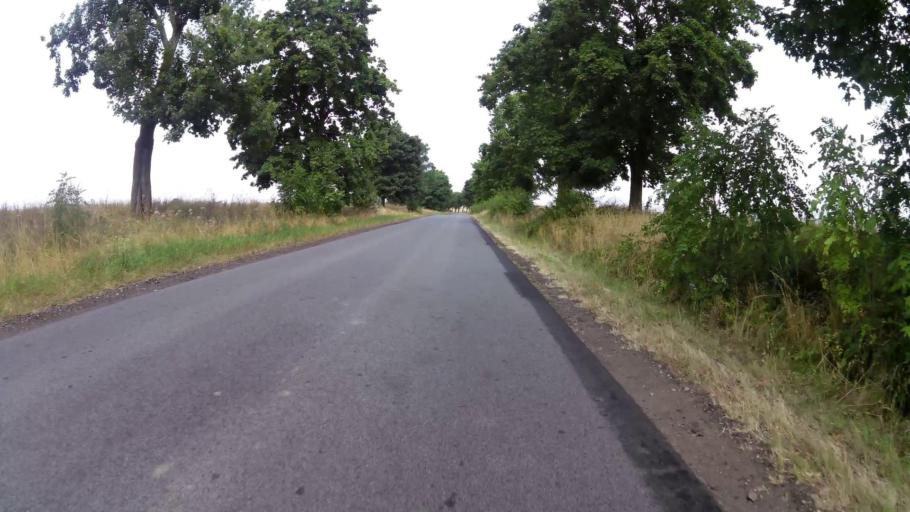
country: PL
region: West Pomeranian Voivodeship
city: Trzcinsko Zdroj
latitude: 52.9484
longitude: 14.6339
